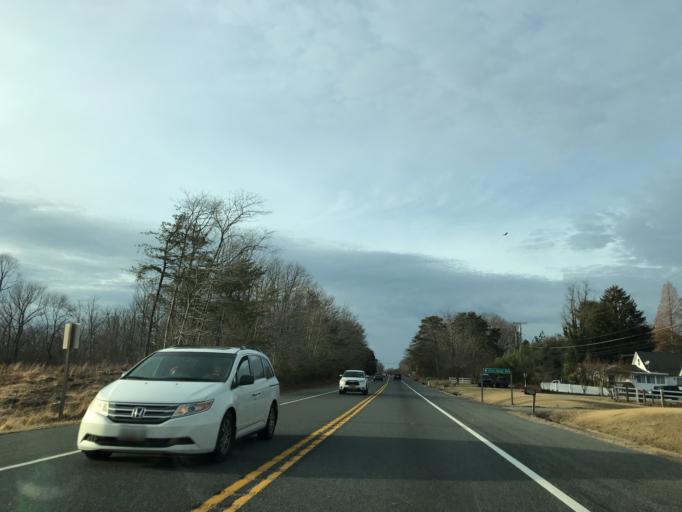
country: US
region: Maryland
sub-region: Harford County
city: Joppatowne
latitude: 39.4552
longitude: -76.3578
